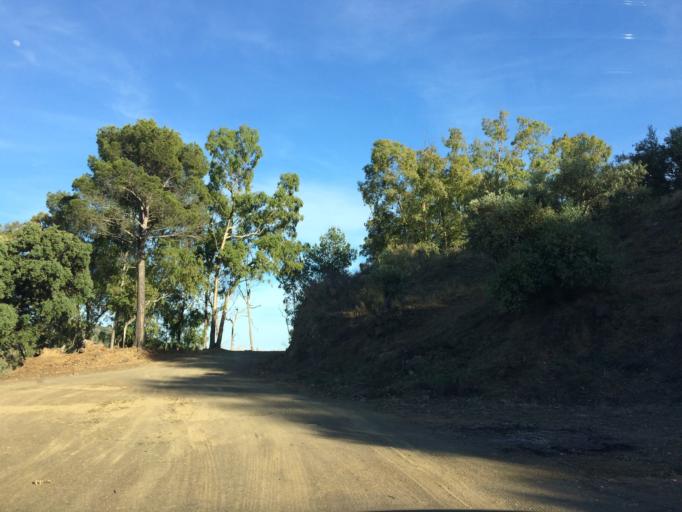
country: ES
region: Andalusia
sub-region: Provincia de Malaga
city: Totalan
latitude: 36.7870
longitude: -4.3207
